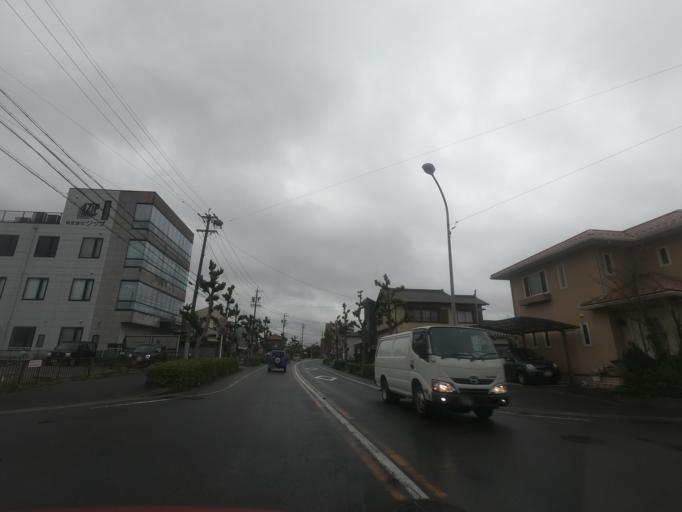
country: JP
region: Aichi
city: Kasugai
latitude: 35.2707
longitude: 136.9802
